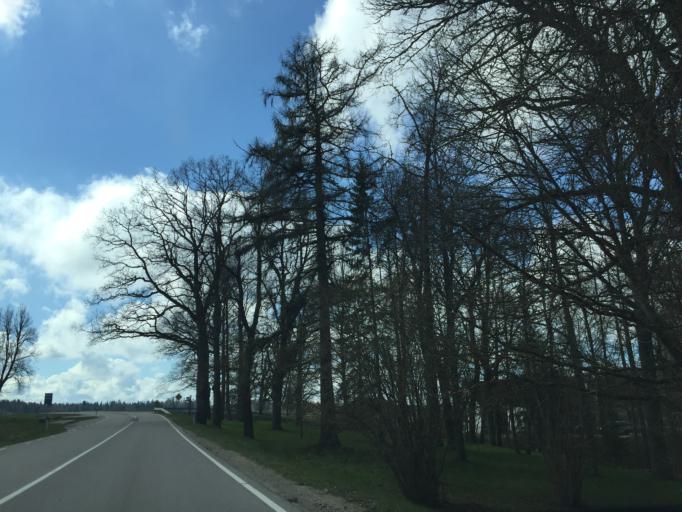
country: LV
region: Apes Novads
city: Ape
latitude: 57.5300
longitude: 26.6982
